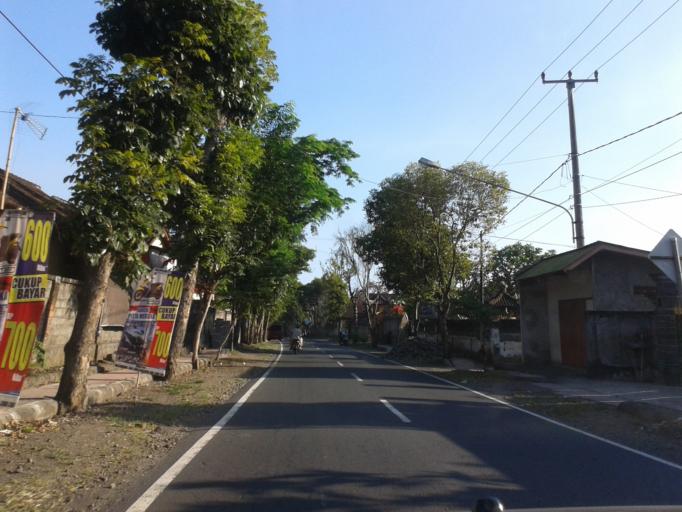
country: ID
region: Bali
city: Banjar Wangsian
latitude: -8.4975
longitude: 115.4032
